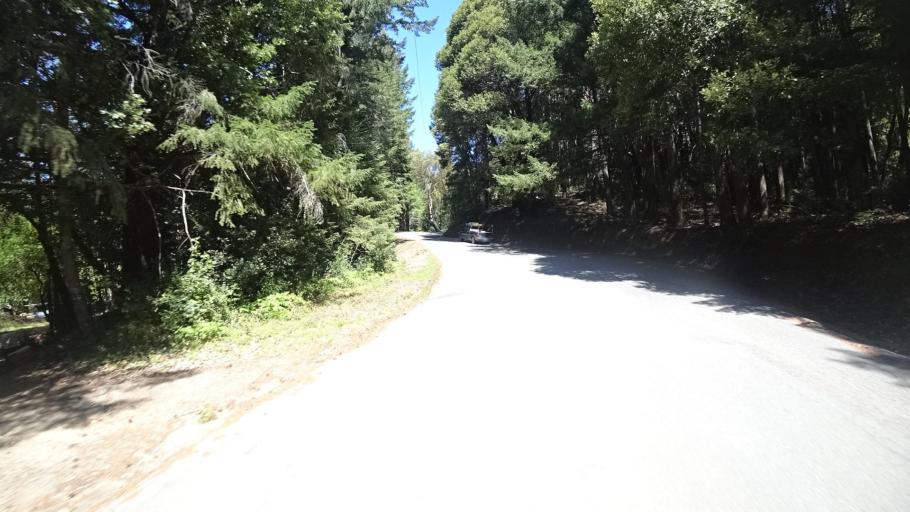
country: US
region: California
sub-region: Humboldt County
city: Redway
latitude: 40.0906
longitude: -123.9489
